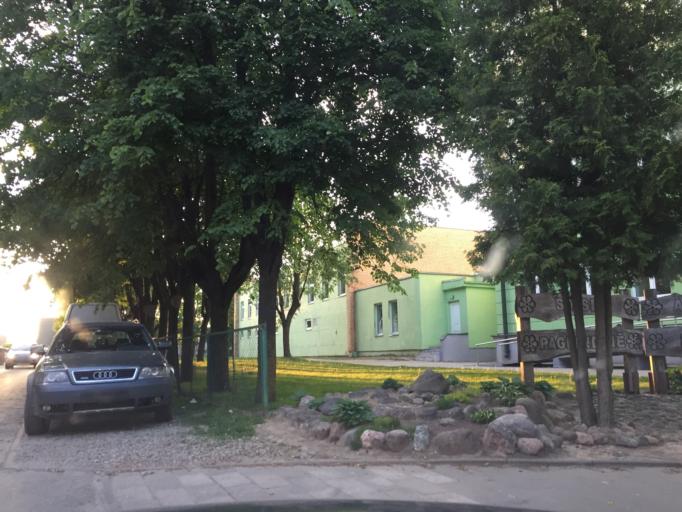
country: LT
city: Kursenai
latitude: 56.0042
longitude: 22.9418
